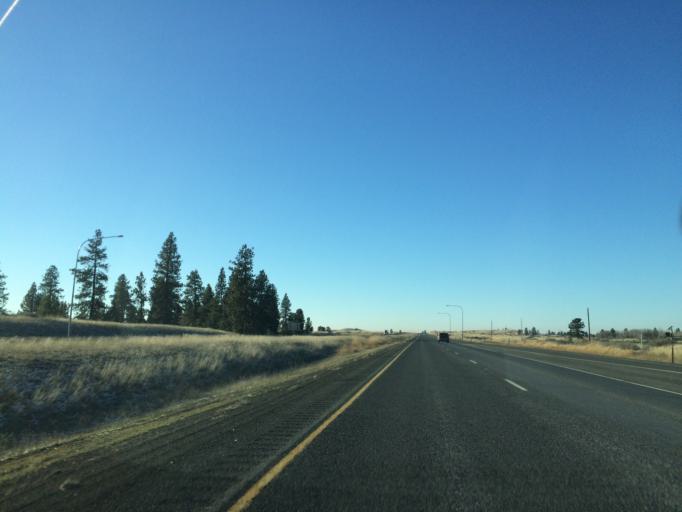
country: US
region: Washington
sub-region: Spokane County
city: Medical Lake
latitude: 47.3939
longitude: -117.8444
